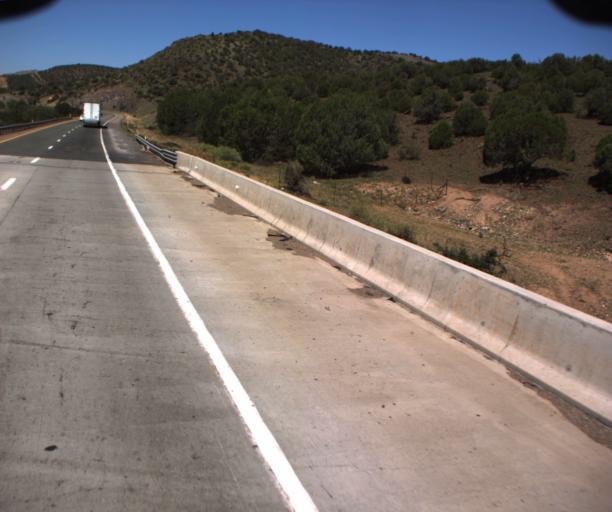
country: US
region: Arizona
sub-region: Mohave County
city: Peach Springs
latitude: 35.1844
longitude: -113.4619
